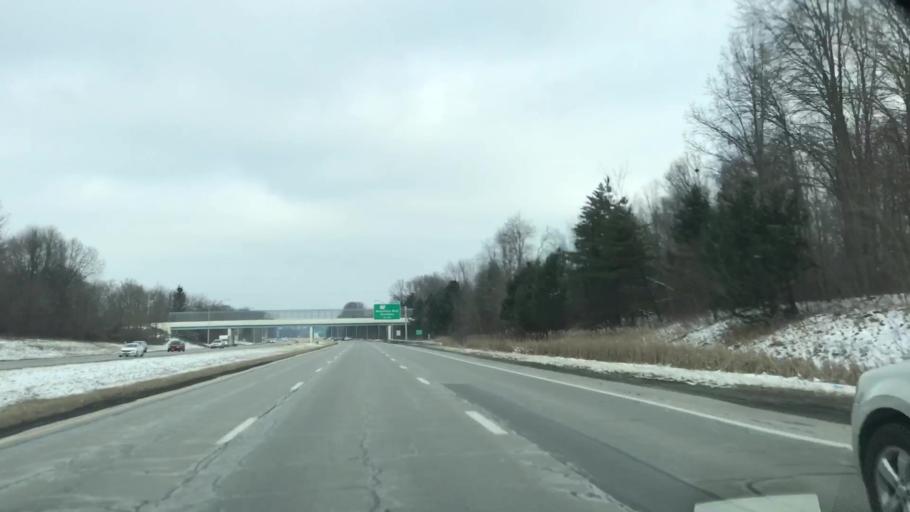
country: US
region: Ohio
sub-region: Mahoning County
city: Struthers
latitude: 41.0485
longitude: -80.6298
